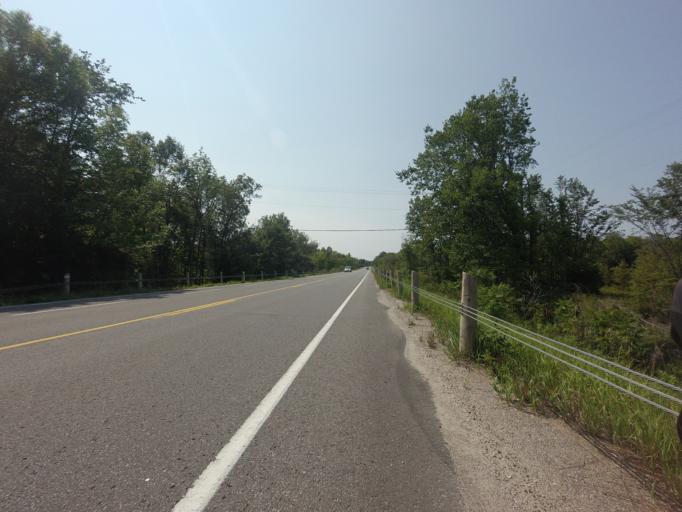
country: CA
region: Ontario
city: Kingston
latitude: 44.6598
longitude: -76.6858
